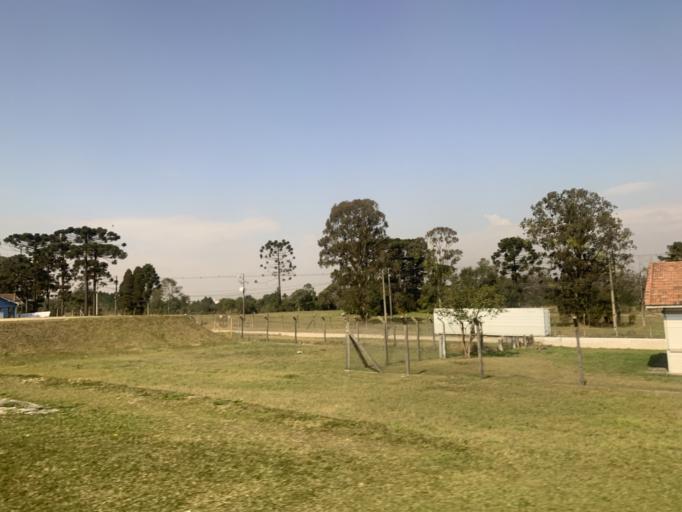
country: BR
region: Parana
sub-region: Sao Jose Dos Pinhais
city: Sao Jose dos Pinhais
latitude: -25.5366
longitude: -49.1796
